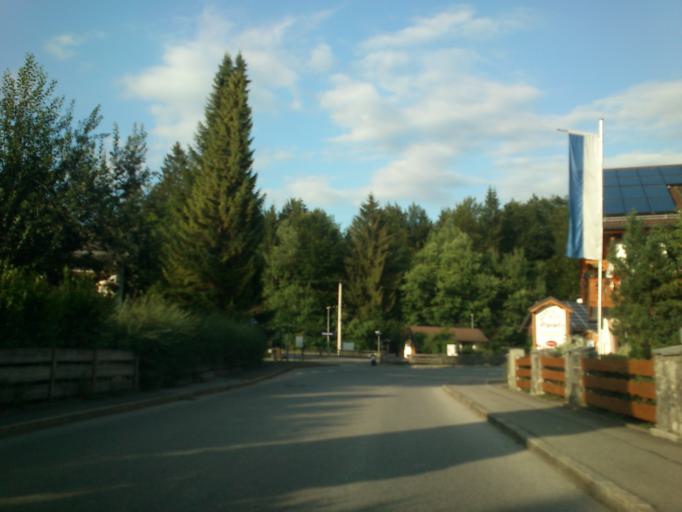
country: DE
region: Bavaria
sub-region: Upper Bavaria
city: Grainau
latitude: 47.4803
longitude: 11.0418
